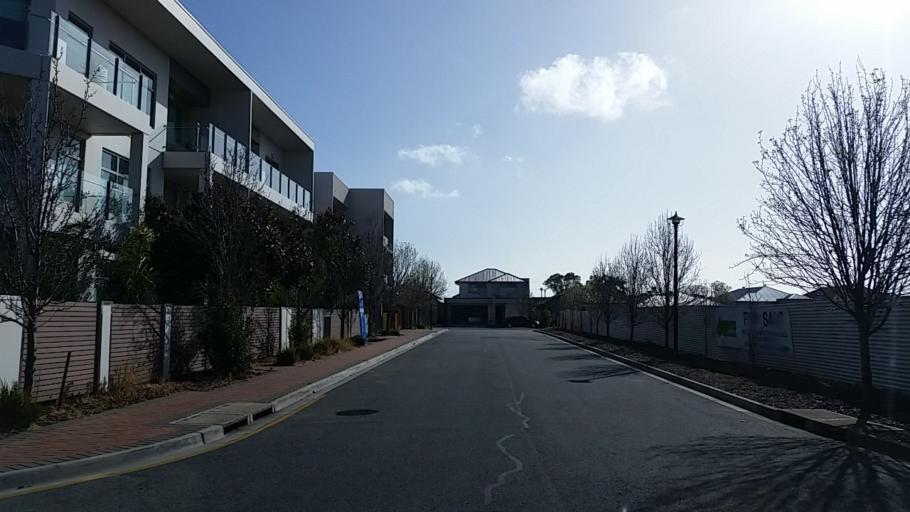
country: AU
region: South Australia
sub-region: Charles Sturt
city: Findon
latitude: -34.9038
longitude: 138.5294
